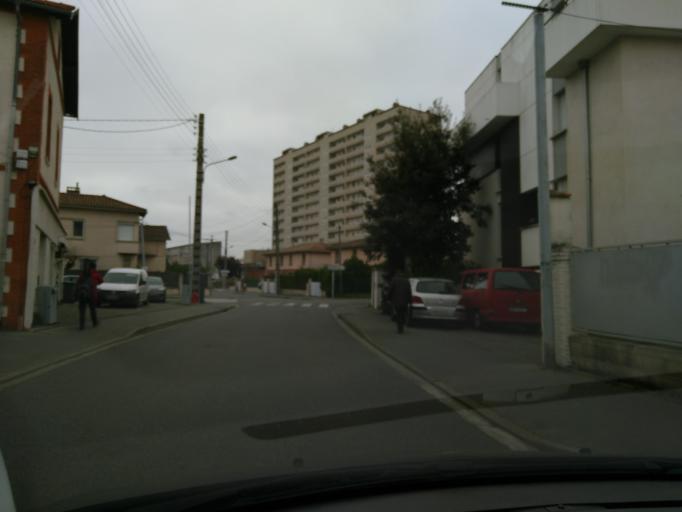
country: FR
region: Midi-Pyrenees
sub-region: Departement de la Haute-Garonne
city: Toulouse
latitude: 43.5816
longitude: 1.4577
